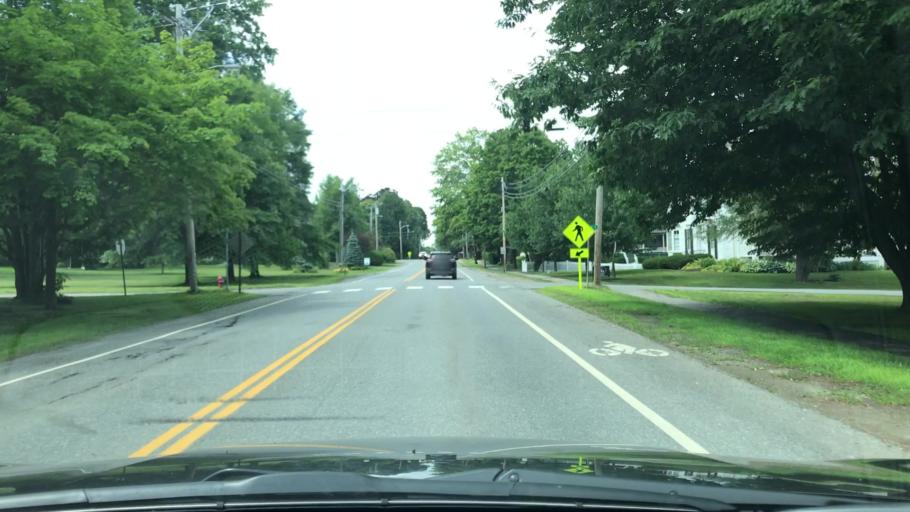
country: US
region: Maine
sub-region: Waldo County
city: Belfast
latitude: 44.4186
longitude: -68.9985
